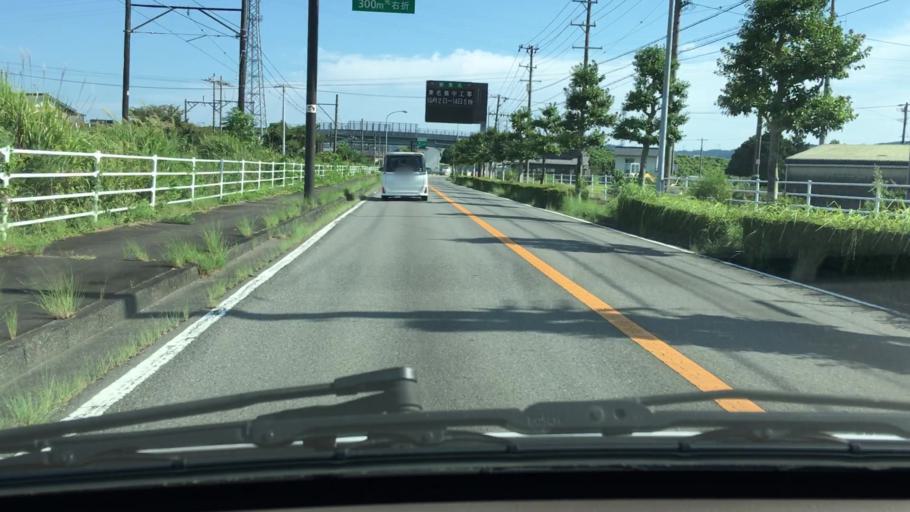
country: JP
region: Shizuoka
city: Kanaya
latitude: 34.8538
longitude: 138.1170
